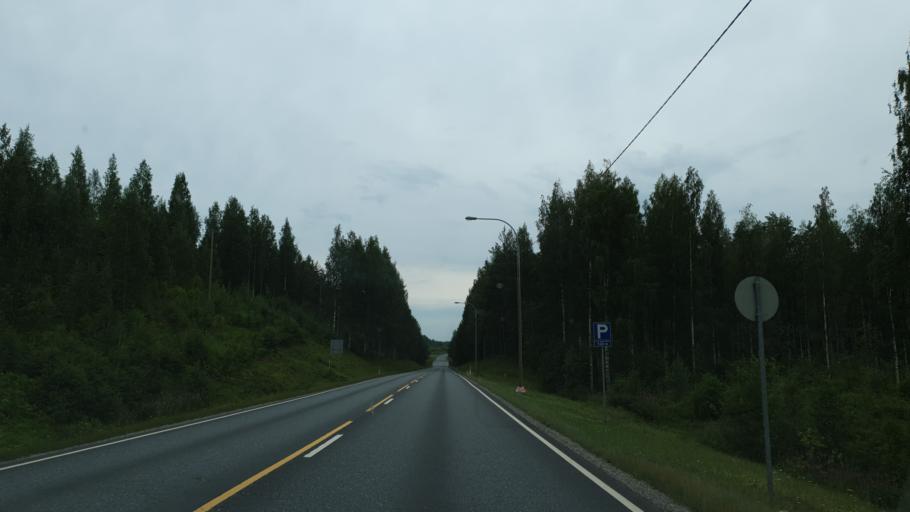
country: FI
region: North Karelia
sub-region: Keski-Karjala
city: Kesaelahti
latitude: 62.0378
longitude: 29.8982
